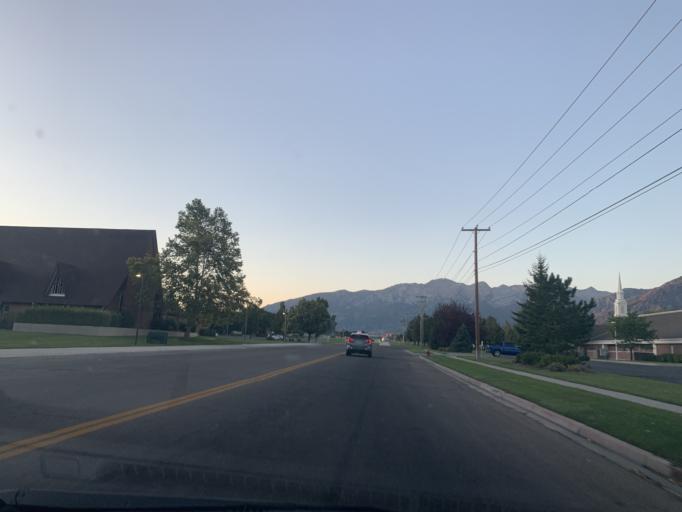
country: US
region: Utah
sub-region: Utah County
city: Cedar Hills
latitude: 40.3941
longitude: -111.7733
